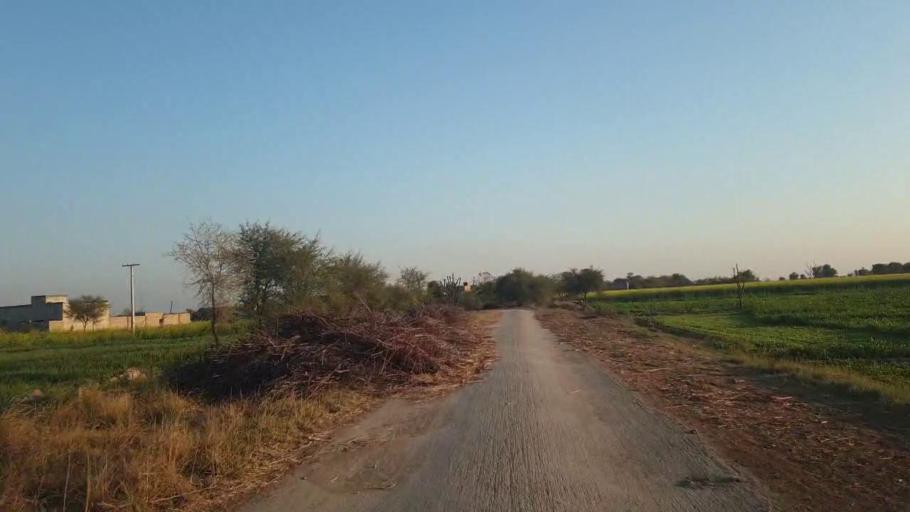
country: PK
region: Sindh
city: Khadro
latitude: 26.0745
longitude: 68.6898
